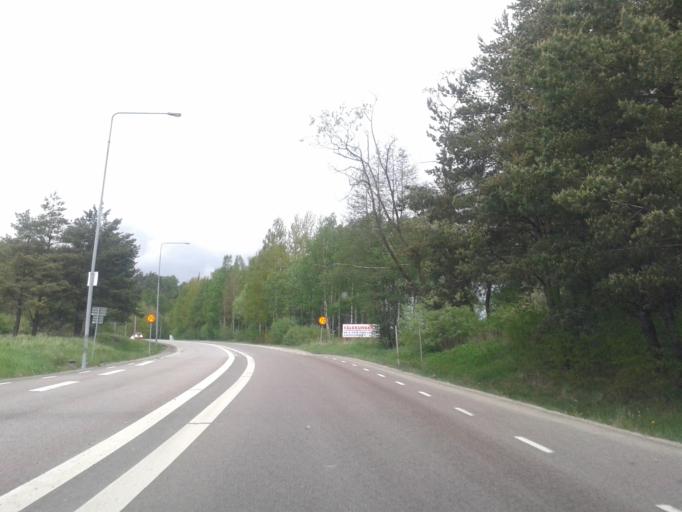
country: SE
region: Vaestra Goetaland
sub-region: Goteborg
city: Eriksbo
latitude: 57.7737
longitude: 12.0503
